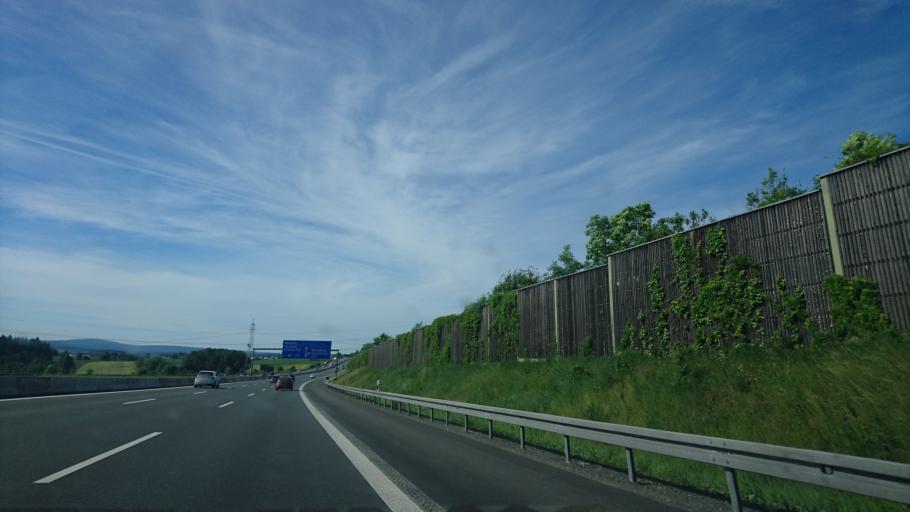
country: DE
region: Bavaria
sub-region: Upper Franconia
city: Munchberg
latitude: 50.2164
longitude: 11.7819
